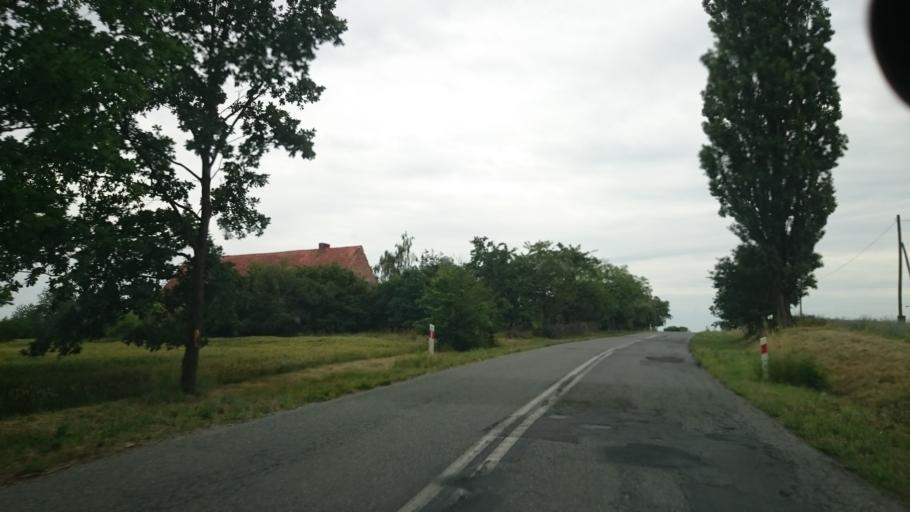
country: PL
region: Lower Silesian Voivodeship
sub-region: Powiat strzelinski
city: Przeworno
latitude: 50.6447
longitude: 17.2108
